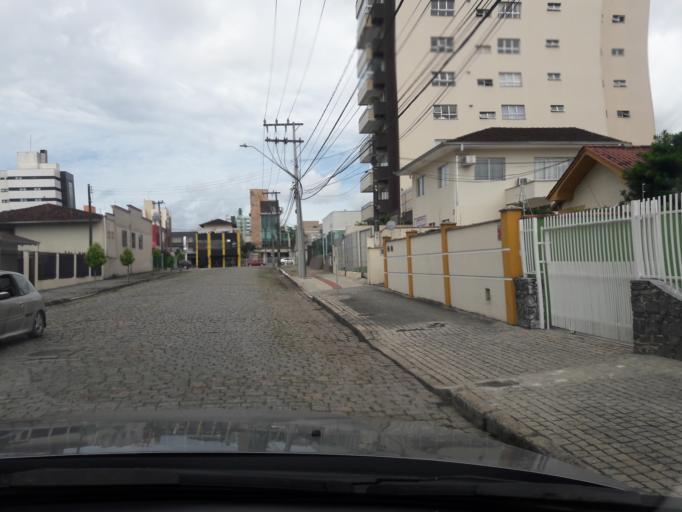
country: BR
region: Santa Catarina
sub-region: Joinville
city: Joinville
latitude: -26.3135
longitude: -48.8466
